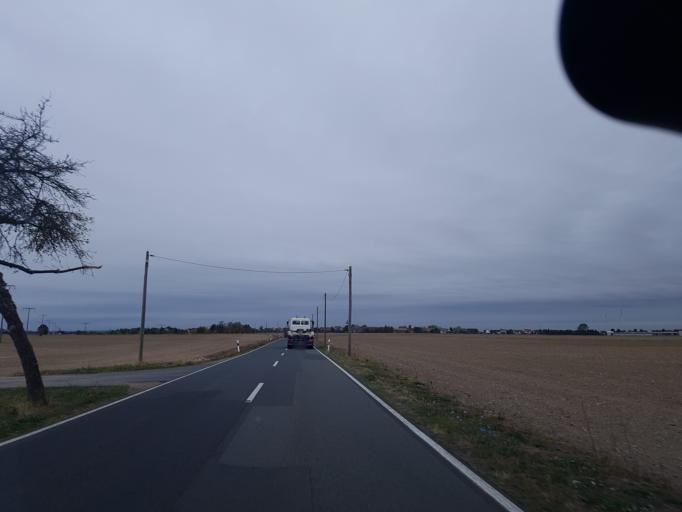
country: DE
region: Saxony
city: Torgau
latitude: 51.6319
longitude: 13.0199
